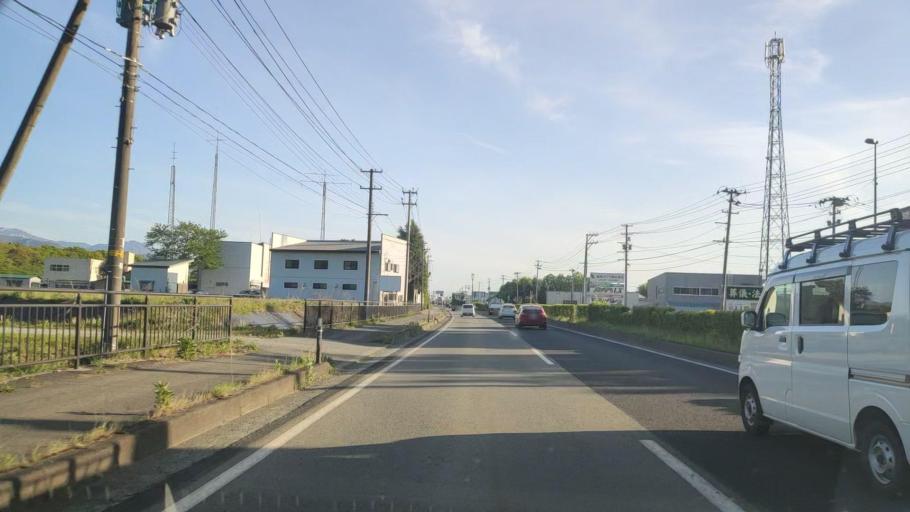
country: JP
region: Yamagata
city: Tendo
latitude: 38.3392
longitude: 140.3722
